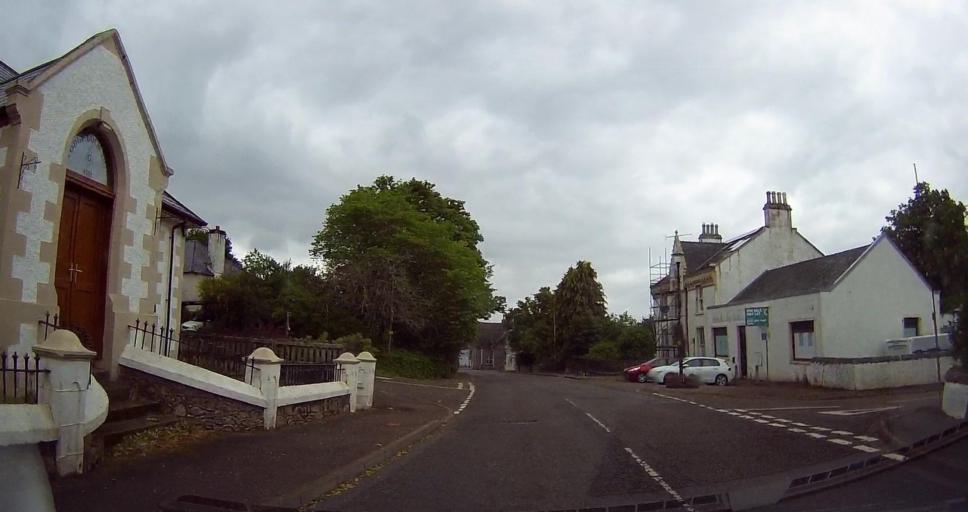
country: GB
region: Scotland
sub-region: Highland
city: Alness
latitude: 58.0236
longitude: -4.3987
